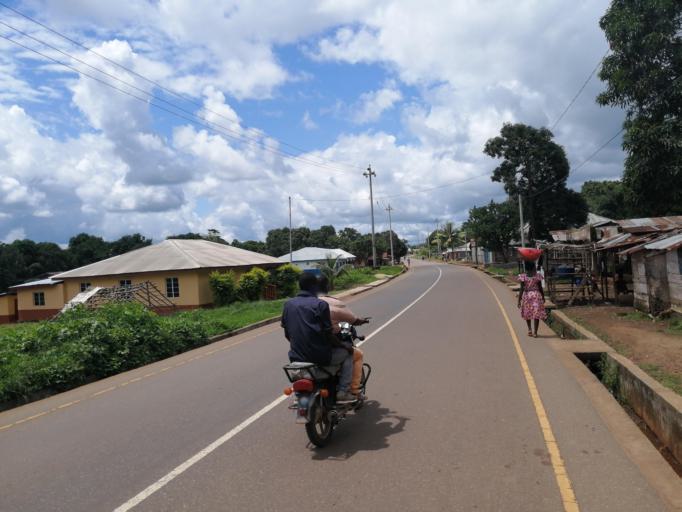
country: SL
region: Northern Province
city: Port Loko
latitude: 8.7696
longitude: -12.7793
